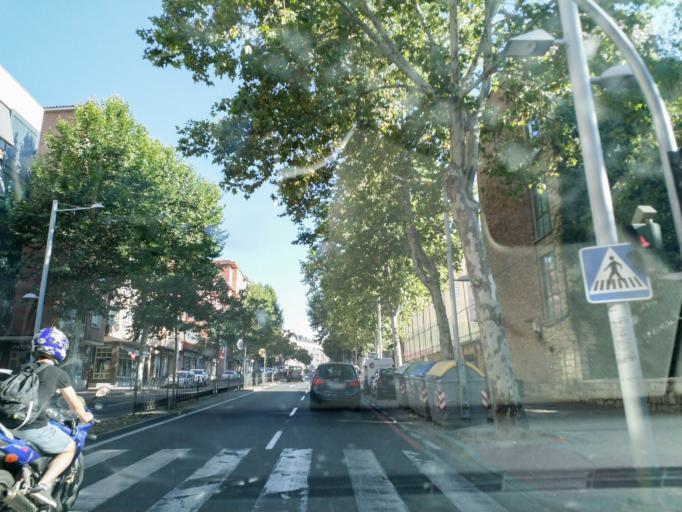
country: ES
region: Castille and Leon
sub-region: Provincia de Segovia
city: Segovia
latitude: 40.9391
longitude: -4.1155
